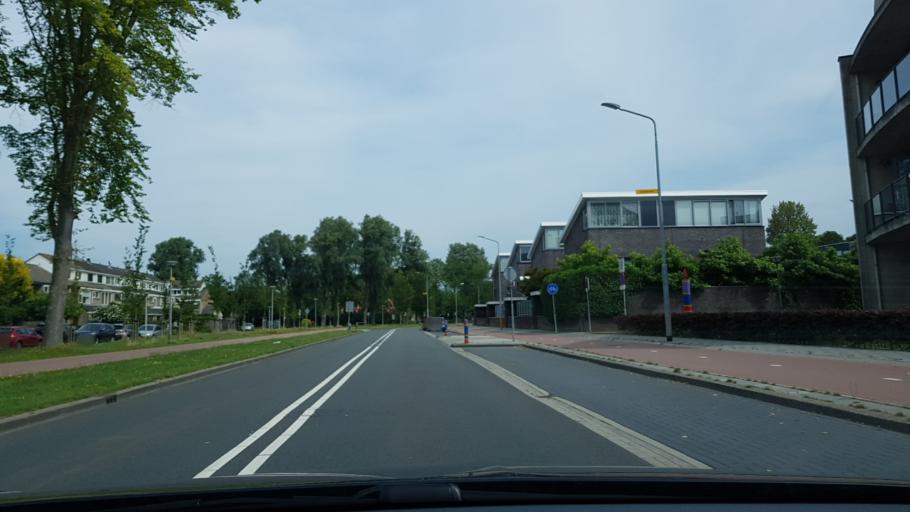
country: NL
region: North Holland
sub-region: Gemeente Castricum
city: Castricum
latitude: 52.5553
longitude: 4.6644
